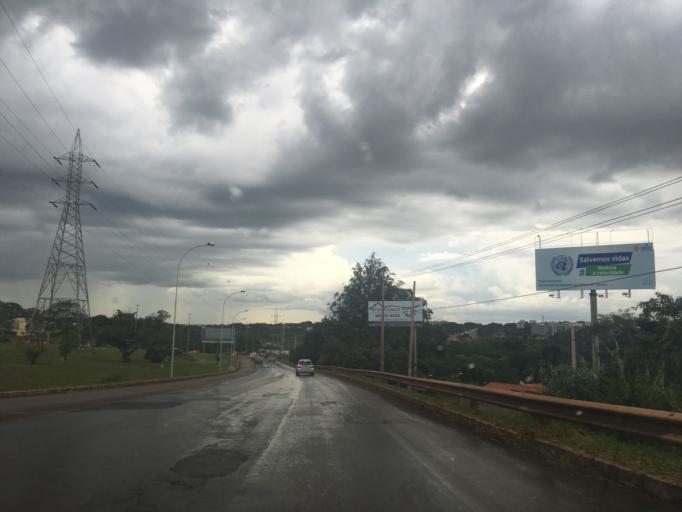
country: BR
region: Federal District
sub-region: Brasilia
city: Brasilia
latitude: -15.7262
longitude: -47.8968
